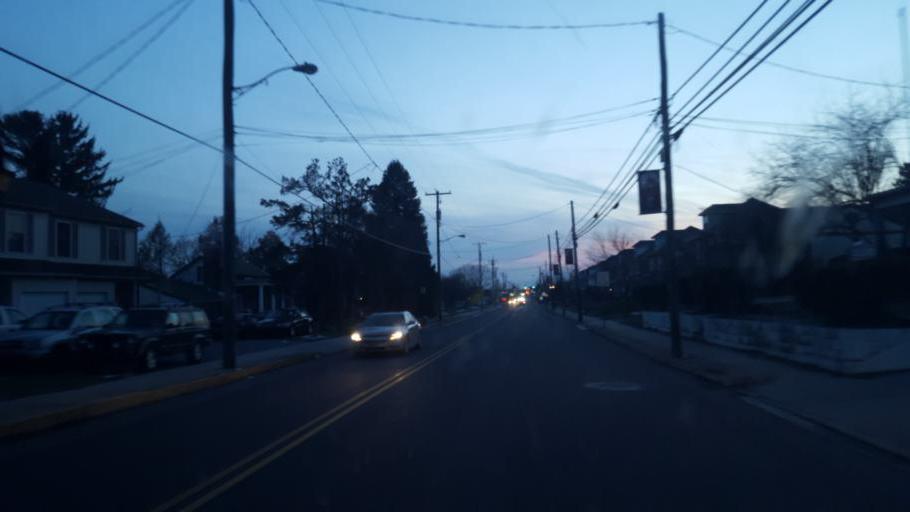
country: US
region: Pennsylvania
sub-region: Lancaster County
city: New Holland
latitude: 40.0974
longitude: -76.1039
